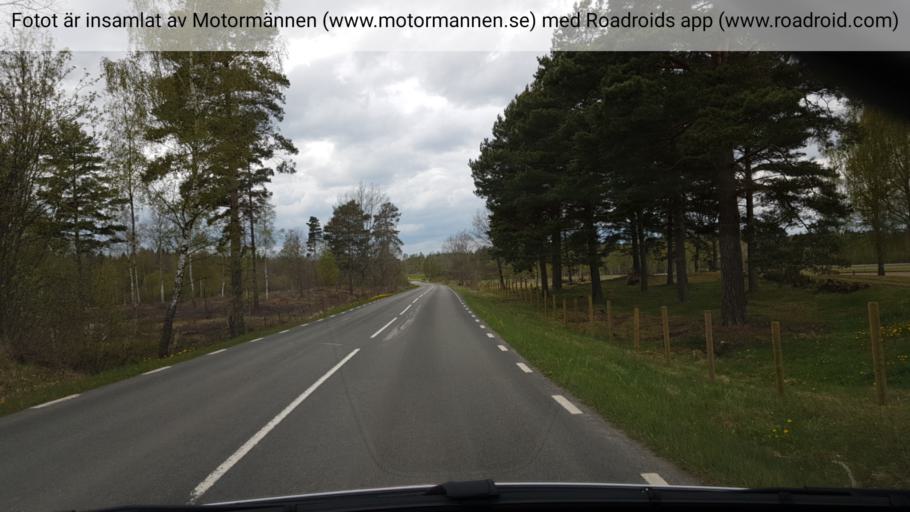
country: SE
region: Vaestra Goetaland
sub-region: Falkopings Kommun
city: Floby
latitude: 58.2106
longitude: 13.3876
